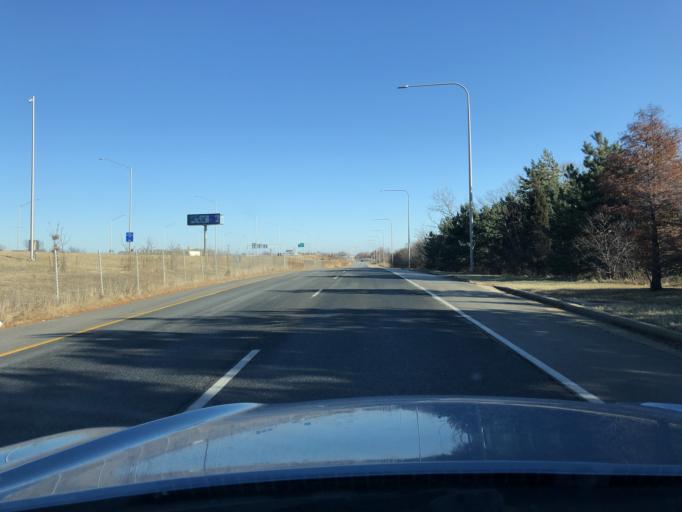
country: US
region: Illinois
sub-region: DuPage County
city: Roselle
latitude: 41.9965
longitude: -88.1078
